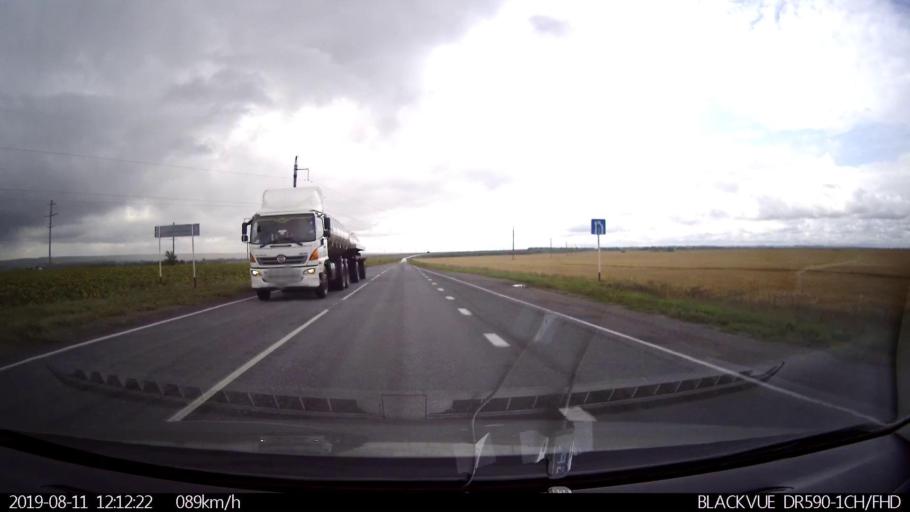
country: RU
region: Ulyanovsk
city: Silikatnyy
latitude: 53.9741
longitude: 47.9970
